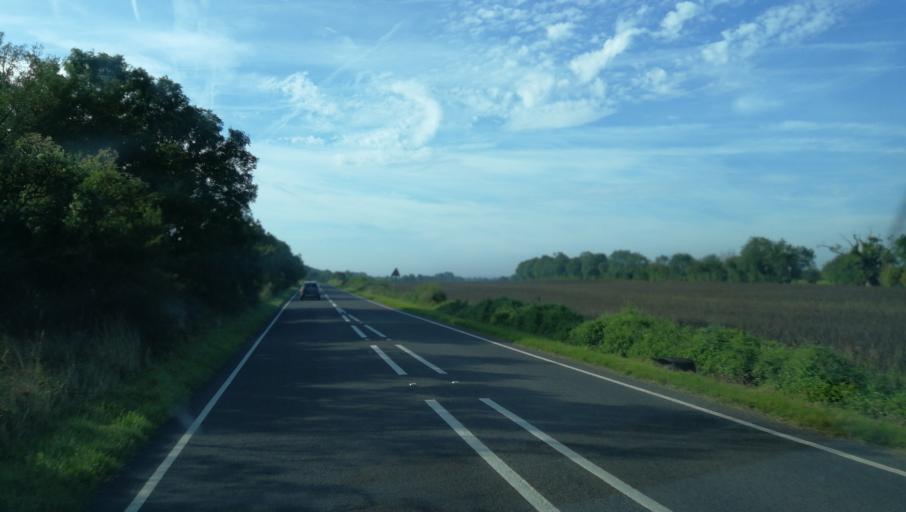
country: GB
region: England
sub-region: Oxfordshire
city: Woodstock
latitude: 51.8981
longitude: -1.3283
